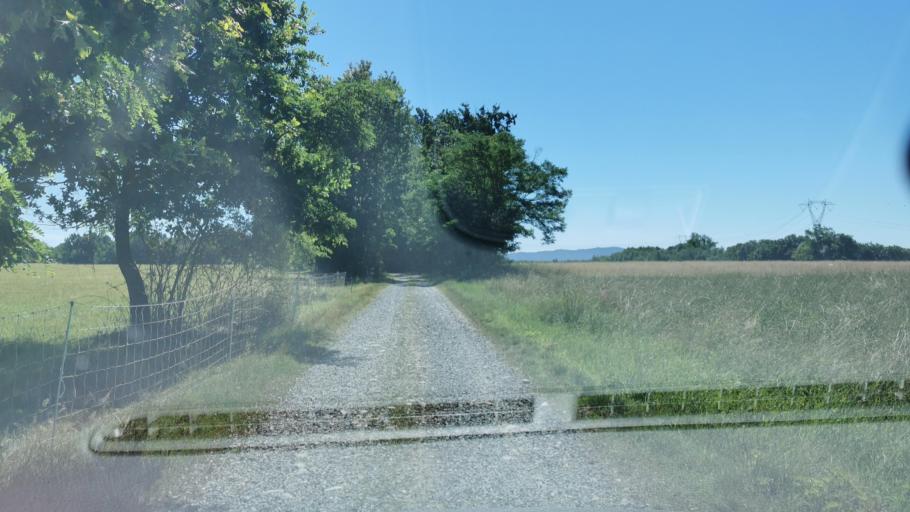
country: IT
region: Piedmont
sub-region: Provincia di Torino
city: San Francesco al Campo
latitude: 45.2339
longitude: 7.6835
